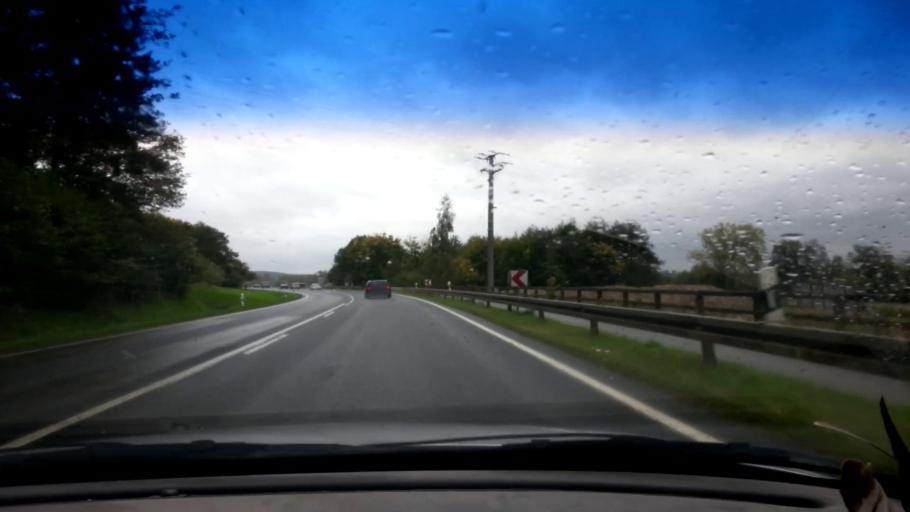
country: DE
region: Bavaria
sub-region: Upper Franconia
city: Viereth-Trunstadt
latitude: 49.9212
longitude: 10.7975
